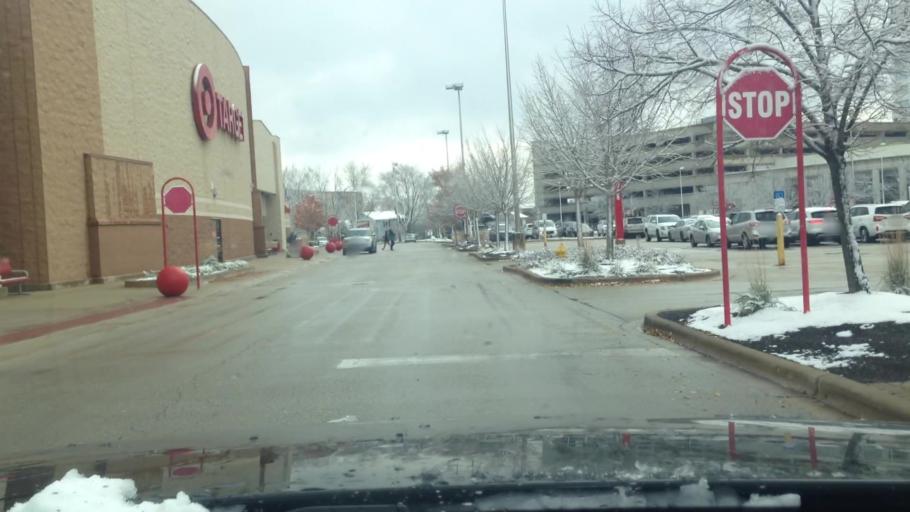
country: US
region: Illinois
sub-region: DuPage County
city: Lombard
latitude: 41.8446
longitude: -88.0038
